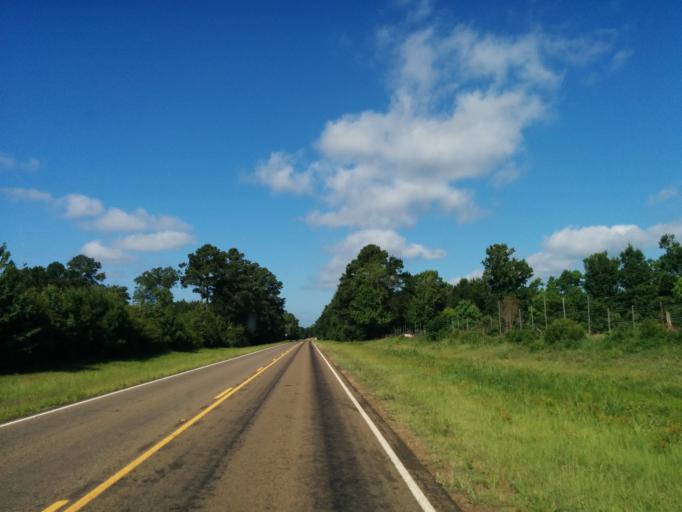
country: US
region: Texas
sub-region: Sabine County
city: Milam
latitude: 31.4159
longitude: -93.9848
